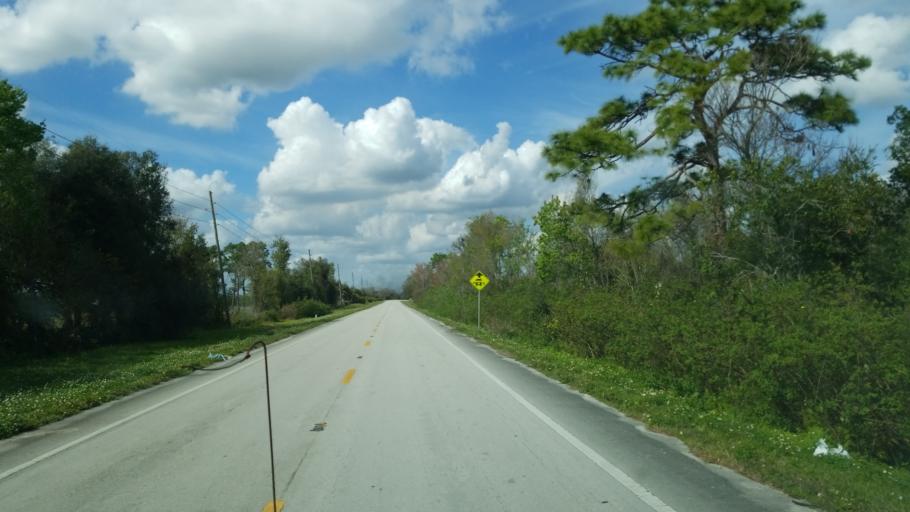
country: US
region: Florida
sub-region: Osceola County
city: Saint Cloud
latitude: 28.0138
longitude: -81.0292
